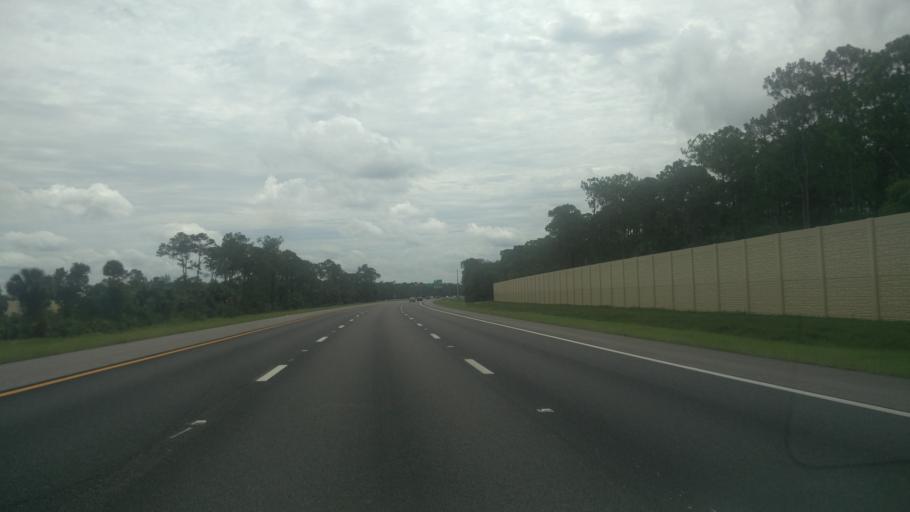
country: US
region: Florida
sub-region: Collier County
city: Golden Gate
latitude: 26.1637
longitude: -81.7058
